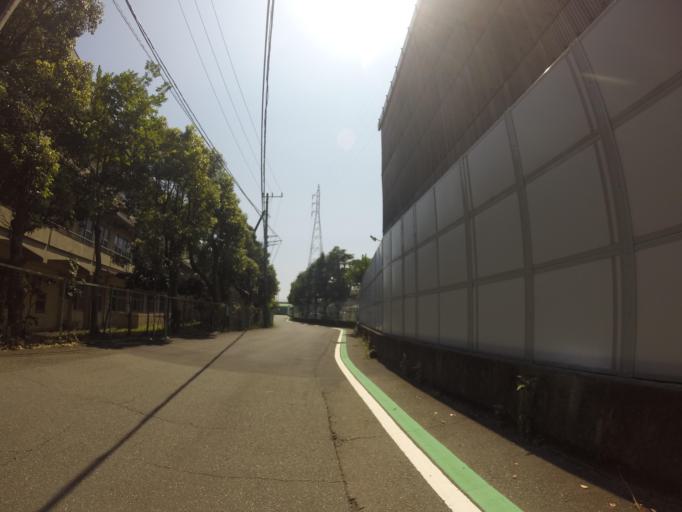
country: JP
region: Shizuoka
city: Numazu
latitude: 35.1155
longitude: 138.8741
